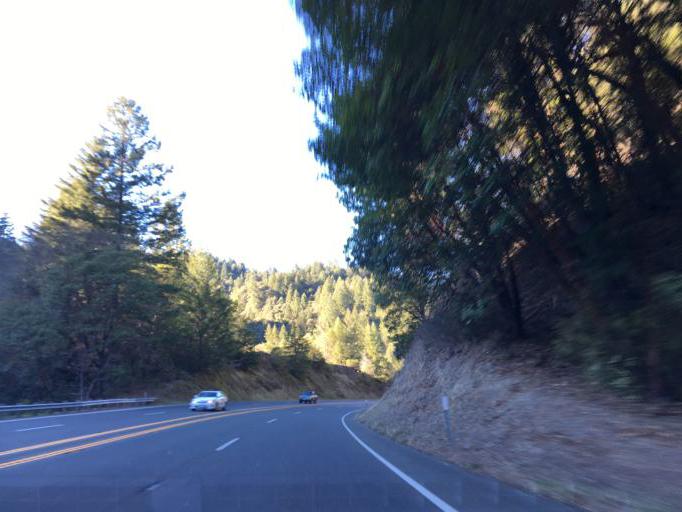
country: US
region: California
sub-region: Mendocino County
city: Laytonville
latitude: 39.5799
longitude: -123.4428
